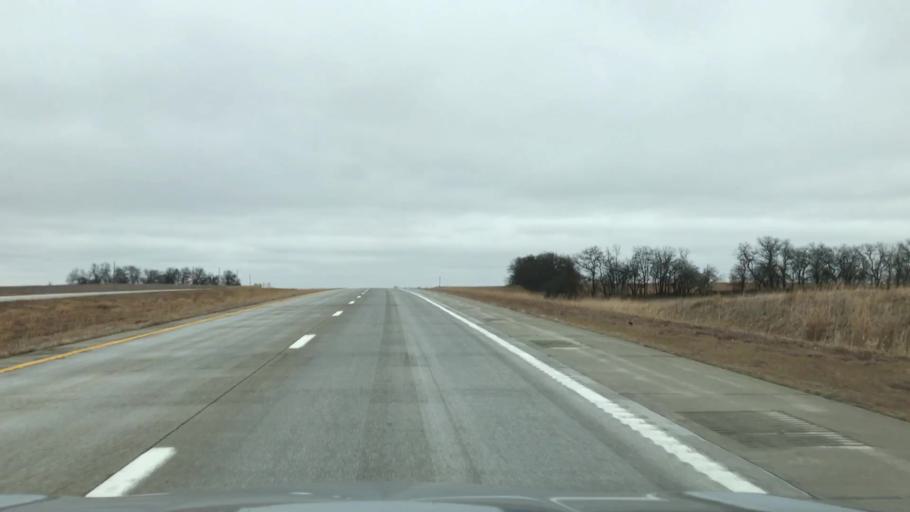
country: US
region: Missouri
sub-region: Livingston County
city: Chillicothe
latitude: 39.7348
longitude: -93.7671
